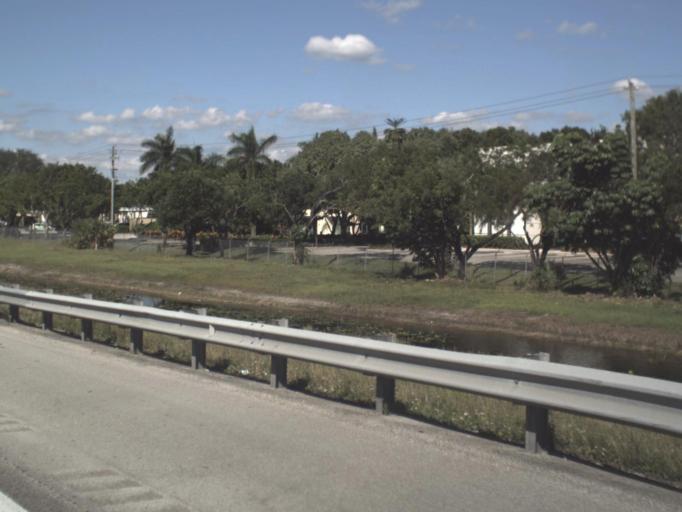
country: US
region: Florida
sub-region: Miami-Dade County
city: Lake Lucerne
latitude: 25.9715
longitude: -80.2812
